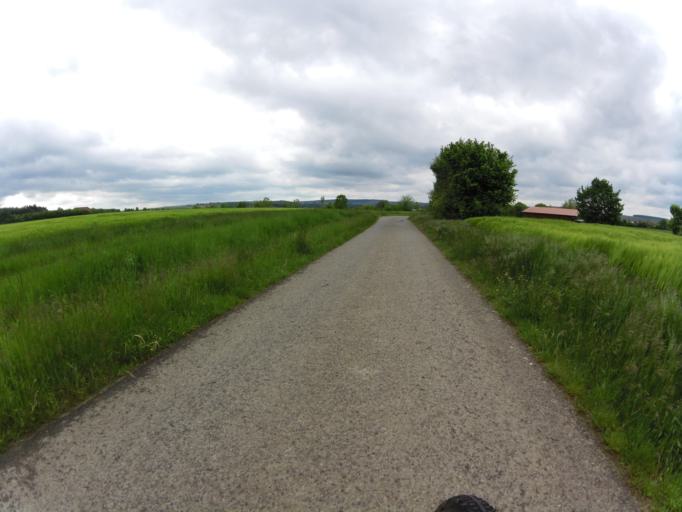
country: DE
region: Bavaria
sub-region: Regierungsbezirk Unterfranken
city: Volkach
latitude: 49.8564
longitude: 10.2436
